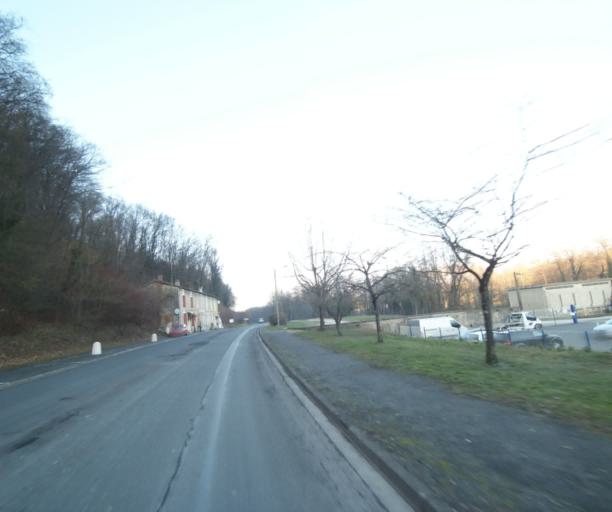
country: FR
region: Champagne-Ardenne
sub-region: Departement de la Haute-Marne
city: Chevillon
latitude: 48.5318
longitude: 5.0968
